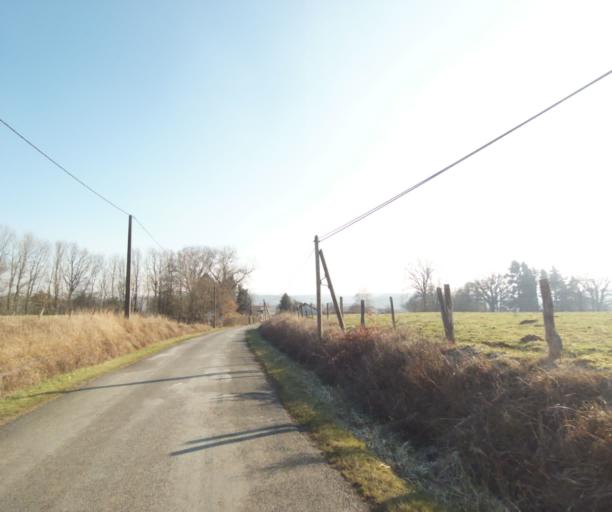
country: FR
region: Champagne-Ardenne
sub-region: Departement de la Haute-Marne
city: Bienville
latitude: 48.5073
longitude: 5.0332
